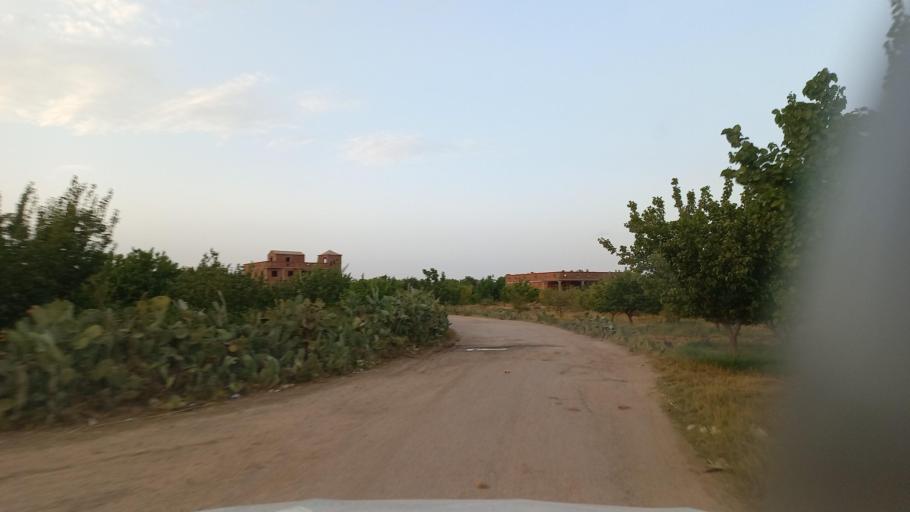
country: TN
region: Al Qasrayn
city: Kasserine
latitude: 35.2737
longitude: 9.0535
